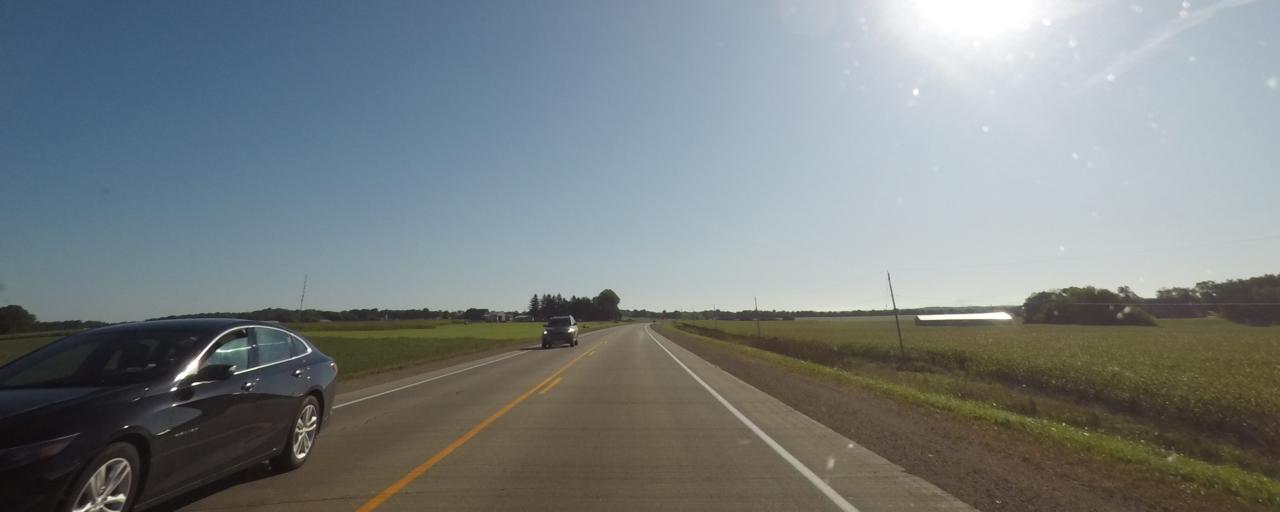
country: US
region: Wisconsin
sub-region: Dane County
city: Deerfield
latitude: 43.0353
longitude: -89.1199
